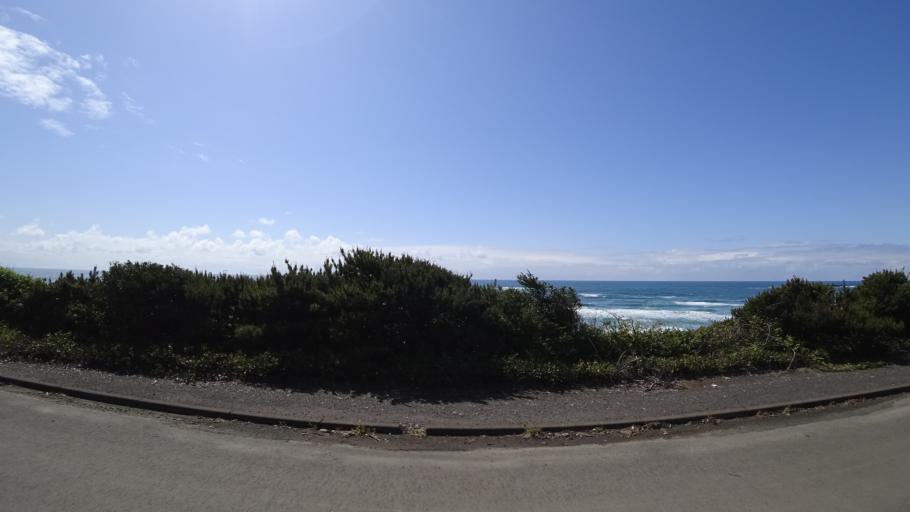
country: US
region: Oregon
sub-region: Lincoln County
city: Newport
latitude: 44.7217
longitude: -124.0585
